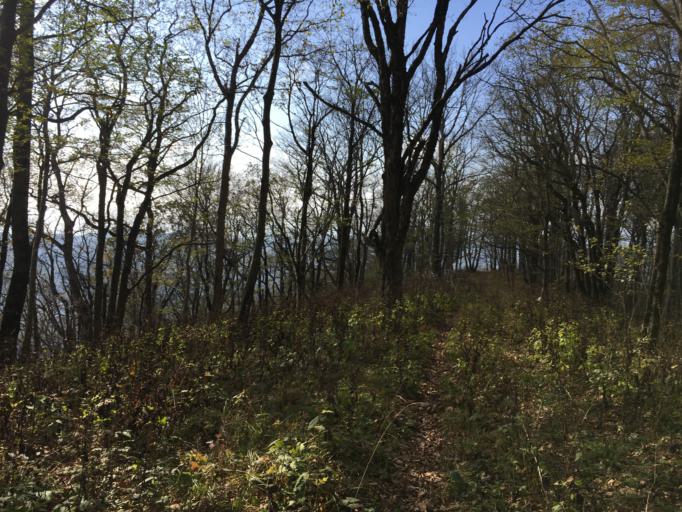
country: RU
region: Krasnodarskiy
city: Nebug
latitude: 44.2423
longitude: 38.9887
